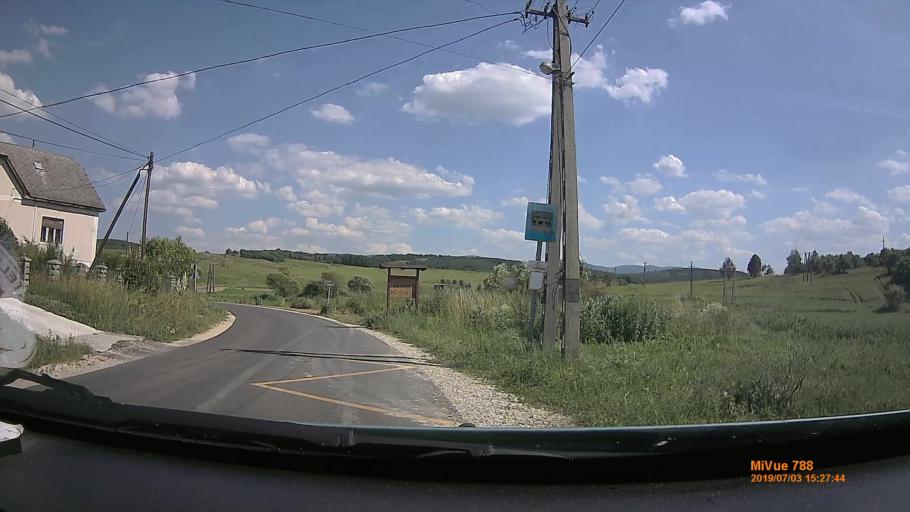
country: HU
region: Heves
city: Szilvasvarad
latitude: 48.1781
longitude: 20.3958
